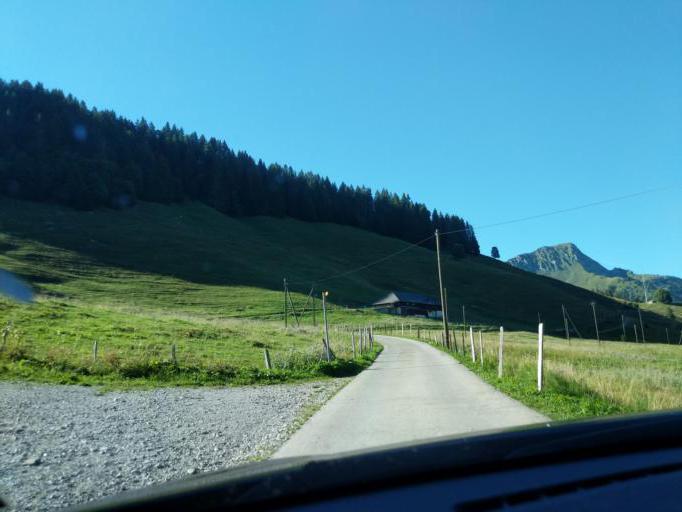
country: CH
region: Fribourg
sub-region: Gruyere District
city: Charmey
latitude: 46.5946
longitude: 7.2674
